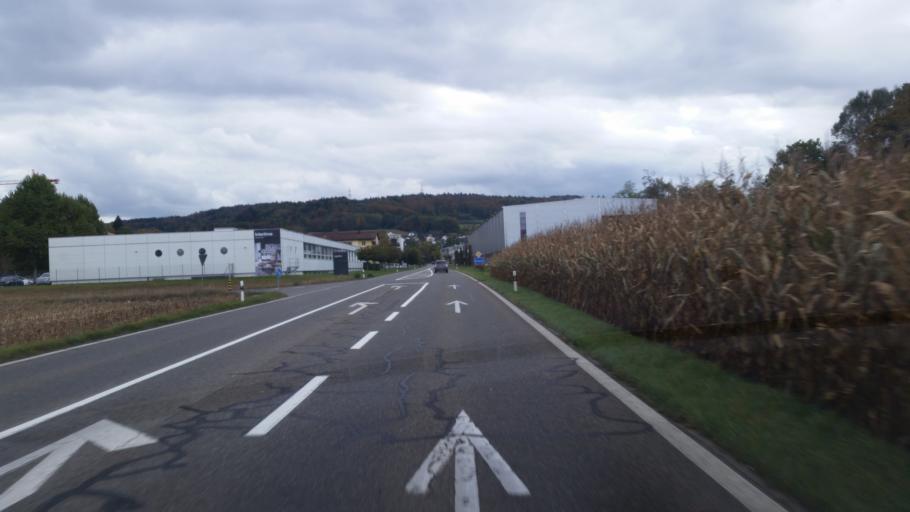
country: CH
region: Aargau
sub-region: Bezirk Zurzach
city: Oberendingen
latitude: 47.5436
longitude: 8.2899
